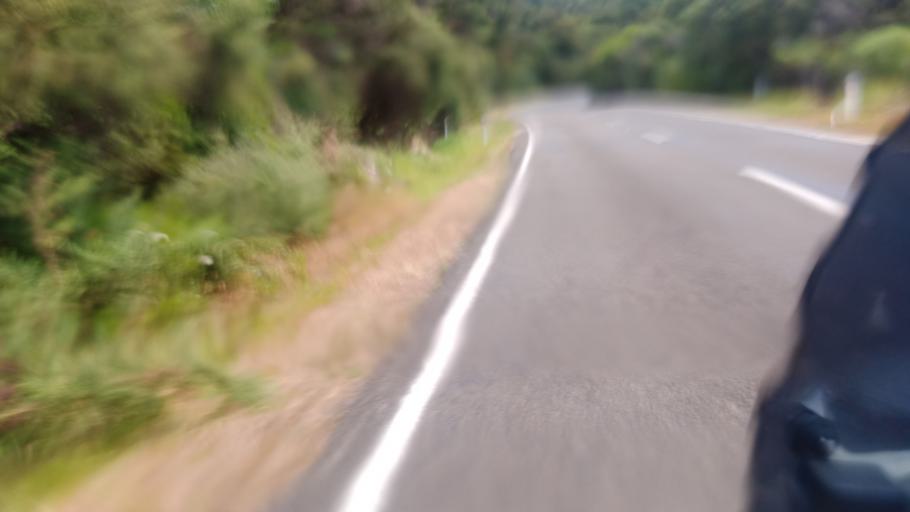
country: NZ
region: Bay of Plenty
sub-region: Opotiki District
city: Opotiki
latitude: -37.5935
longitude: 178.1568
